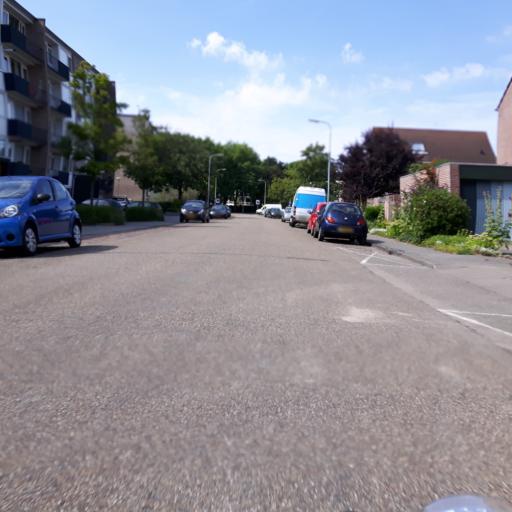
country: NL
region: Zeeland
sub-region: Gemeente Goes
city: Goes
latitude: 51.5072
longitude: 3.8971
